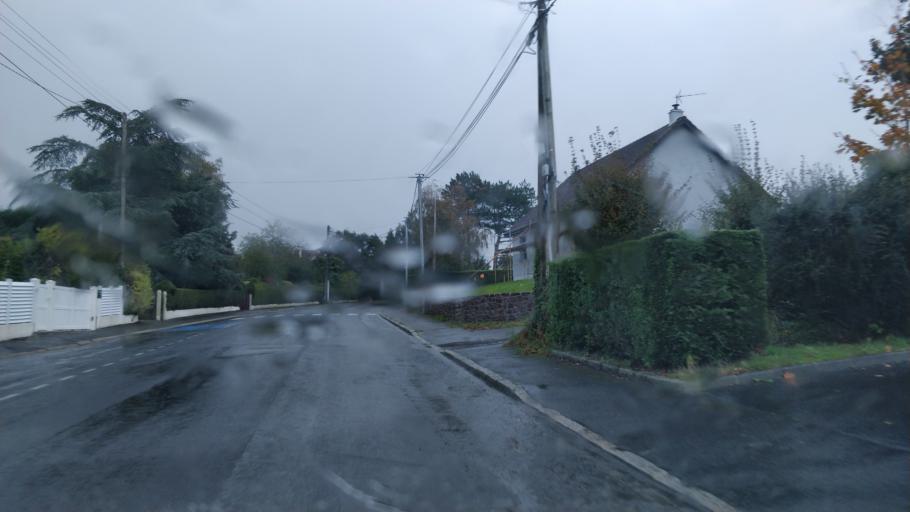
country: FR
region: Lower Normandy
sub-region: Departement de la Manche
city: Brehal
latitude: 48.9010
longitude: -1.5182
